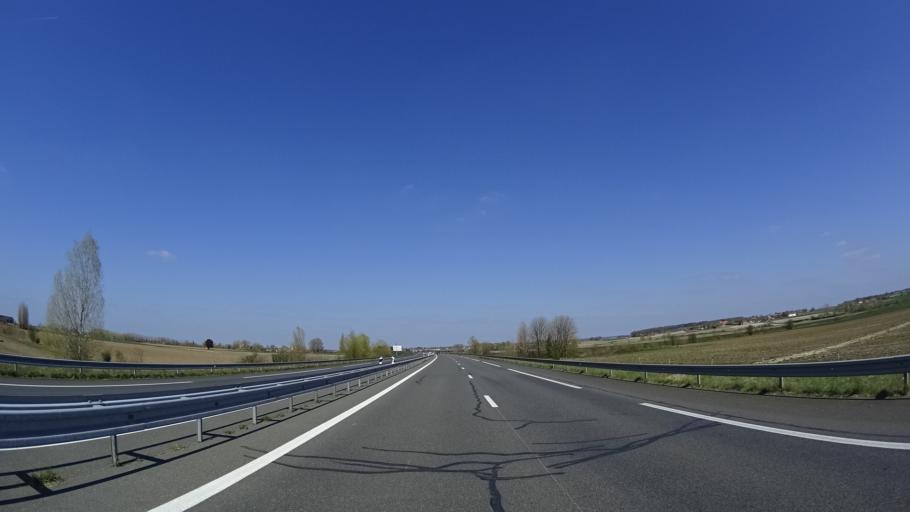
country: FR
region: Pays de la Loire
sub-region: Departement de Maine-et-Loire
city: Saint-Jean
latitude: 47.2637
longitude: -0.3344
